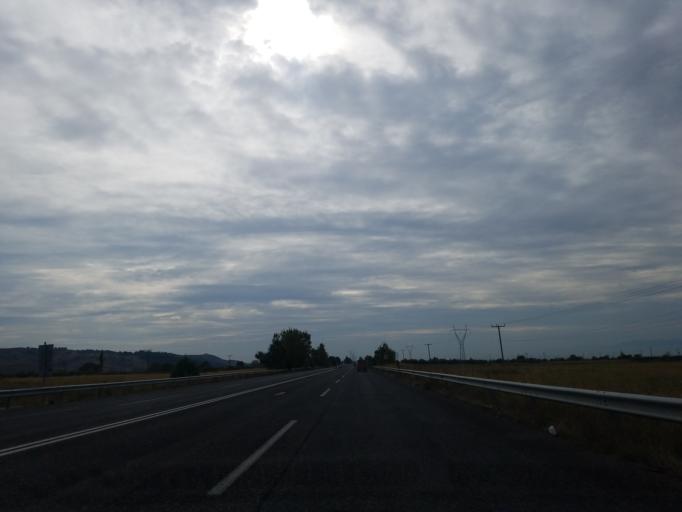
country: GR
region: Thessaly
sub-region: Trikala
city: Vasiliki
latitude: 39.6592
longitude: 21.6761
